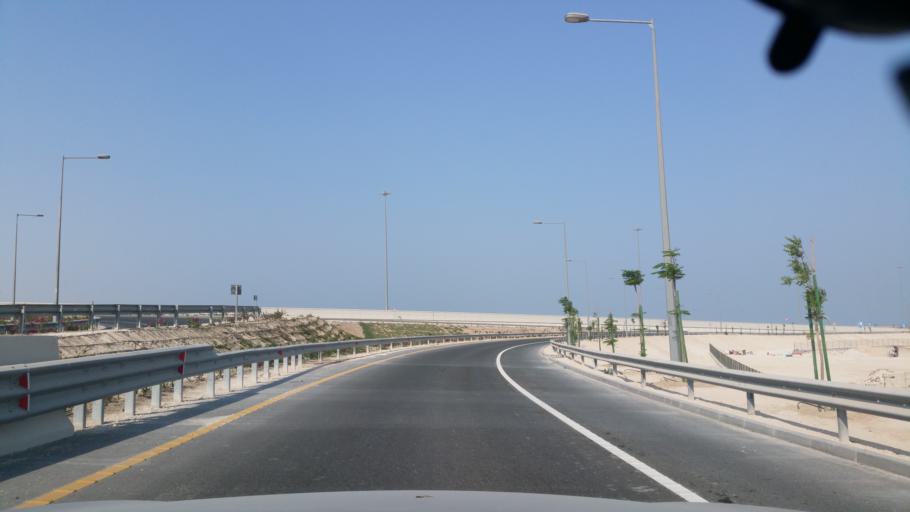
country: QA
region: Baladiyat Umm Salal
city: Umm Salal `Ali
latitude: 25.4553
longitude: 51.4797
